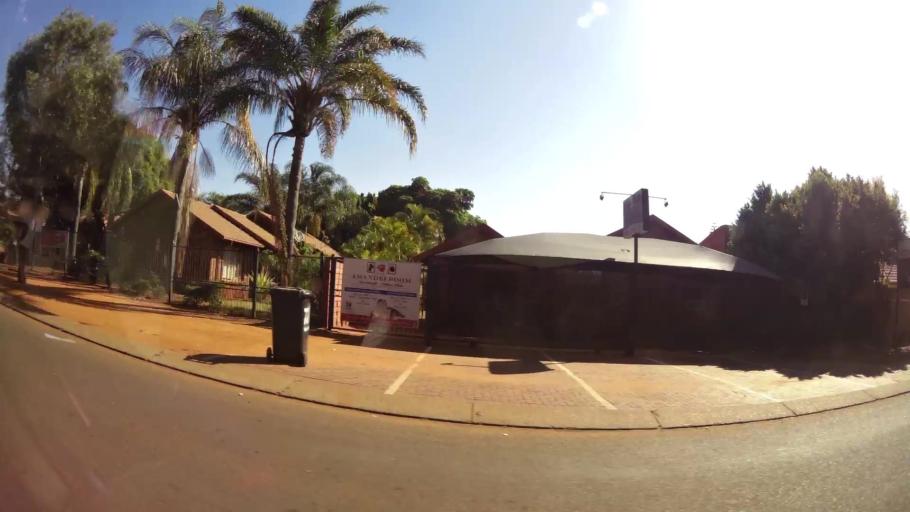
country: ZA
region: Gauteng
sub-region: City of Tshwane Metropolitan Municipality
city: Pretoria
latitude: -25.6551
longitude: 28.2517
